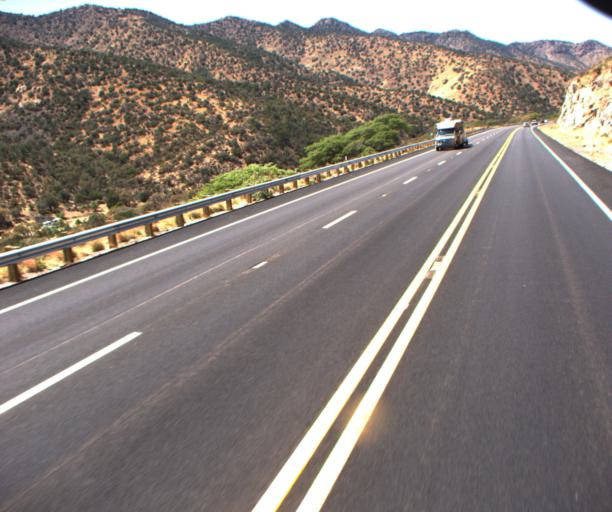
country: US
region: Arizona
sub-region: Cochise County
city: Bisbee
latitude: 31.4658
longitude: -109.9542
